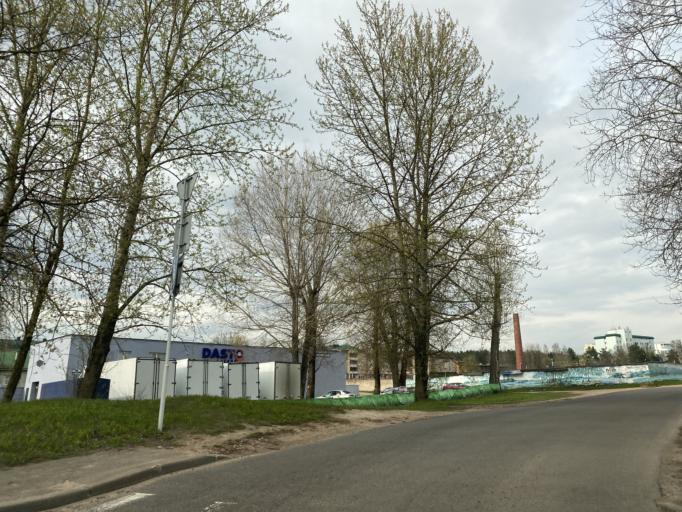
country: BY
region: Minsk
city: Vyaliki Trastsyanets
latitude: 53.9204
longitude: 27.6723
